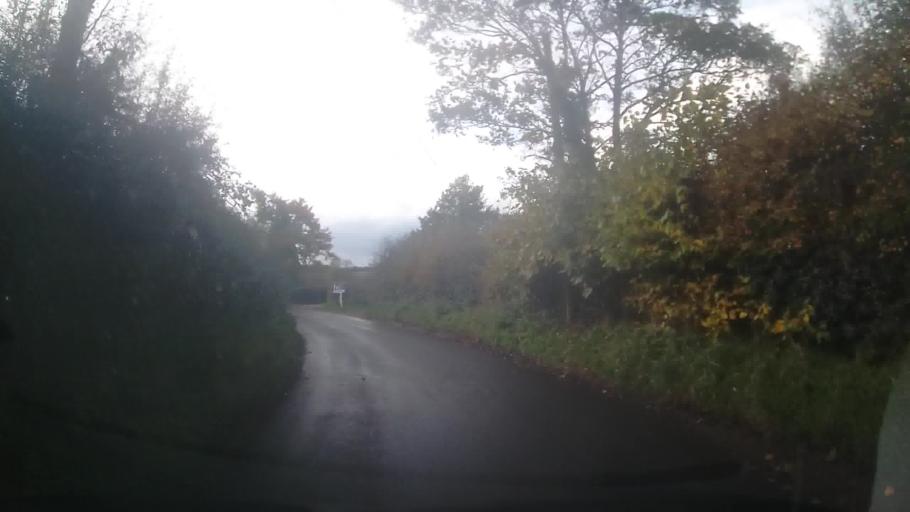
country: GB
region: England
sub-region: Shropshire
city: Whitchurch
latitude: 52.9409
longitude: -2.7180
